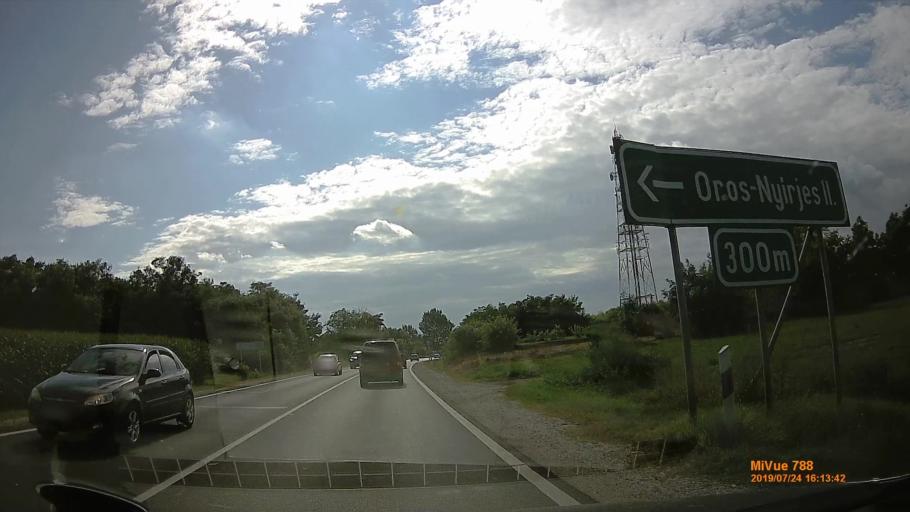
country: HU
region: Szabolcs-Szatmar-Bereg
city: Nyirpazony
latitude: 47.9483
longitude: 21.8029
